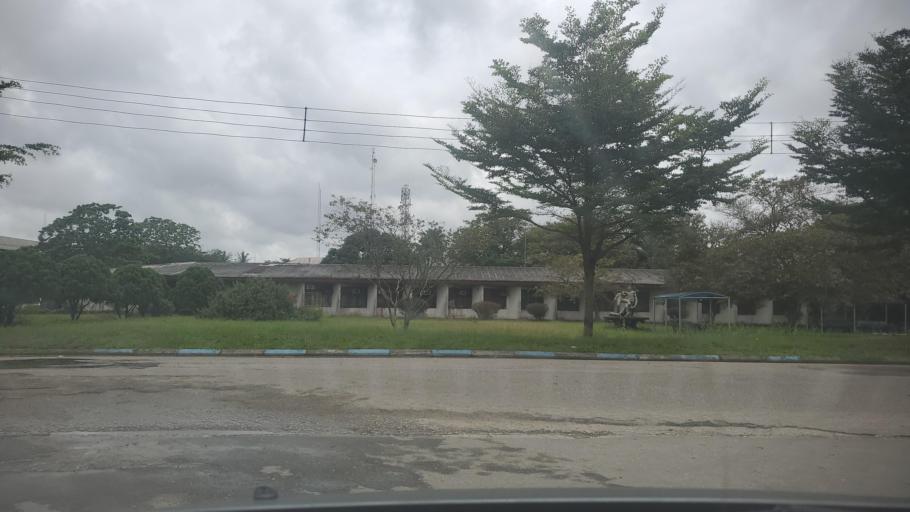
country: NG
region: Rivers
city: Emuoha
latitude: 4.9014
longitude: 6.9227
